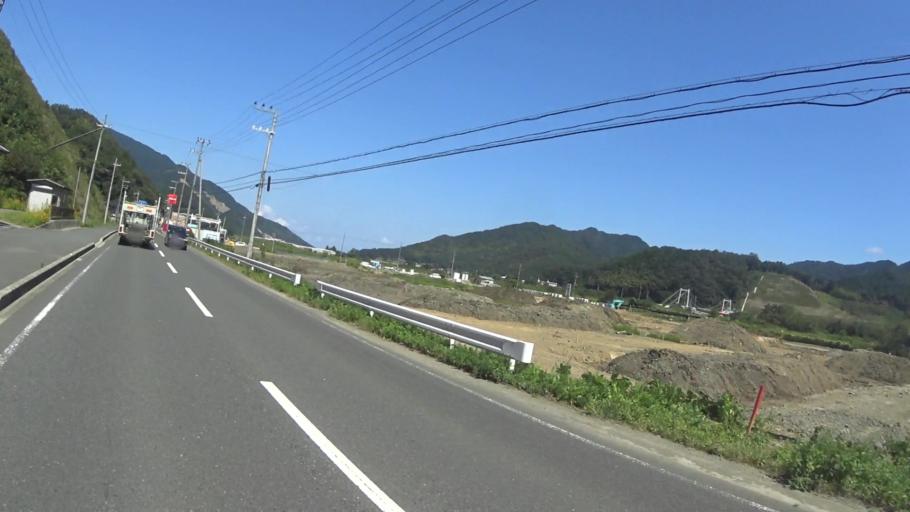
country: JP
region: Kyoto
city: Maizuru
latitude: 35.4636
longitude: 135.2788
